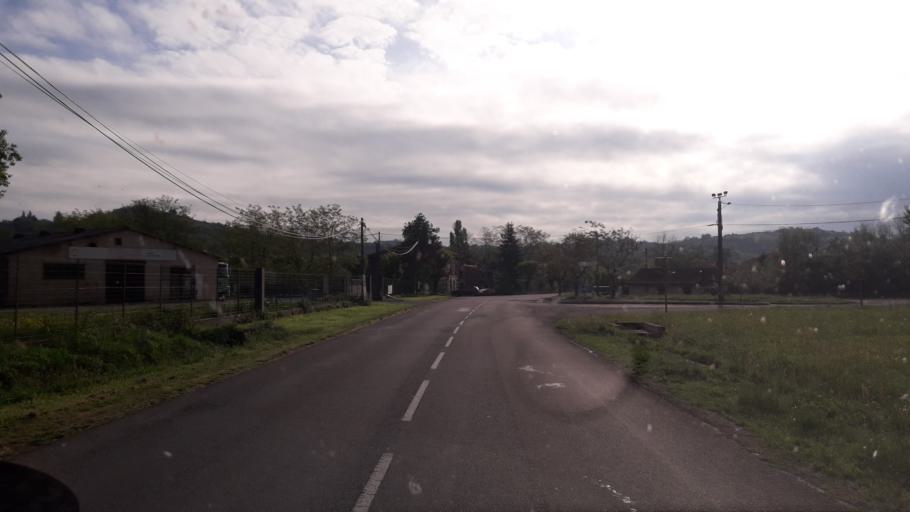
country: FR
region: Midi-Pyrenees
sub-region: Departement de la Haute-Garonne
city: Montesquieu-Volvestre
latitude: 43.2052
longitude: 1.2240
